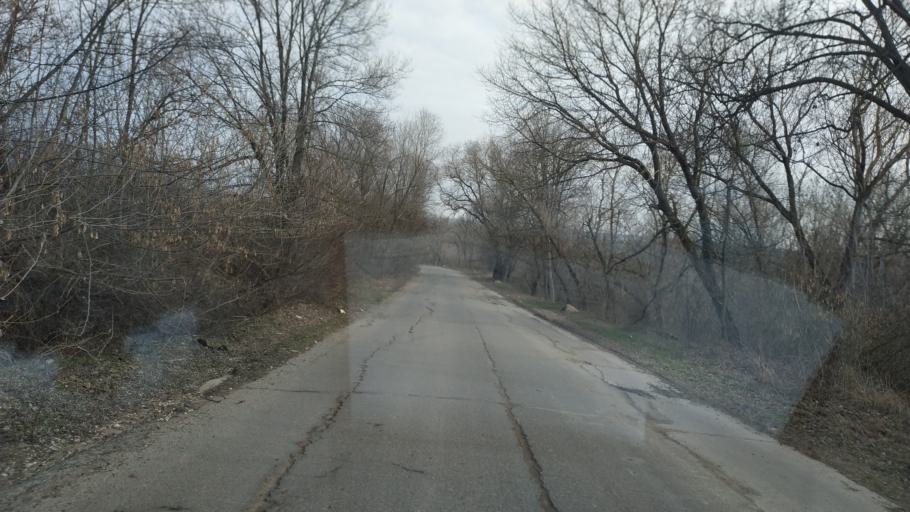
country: MD
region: Chisinau
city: Vadul lui Voda
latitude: 46.9971
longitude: 29.1100
